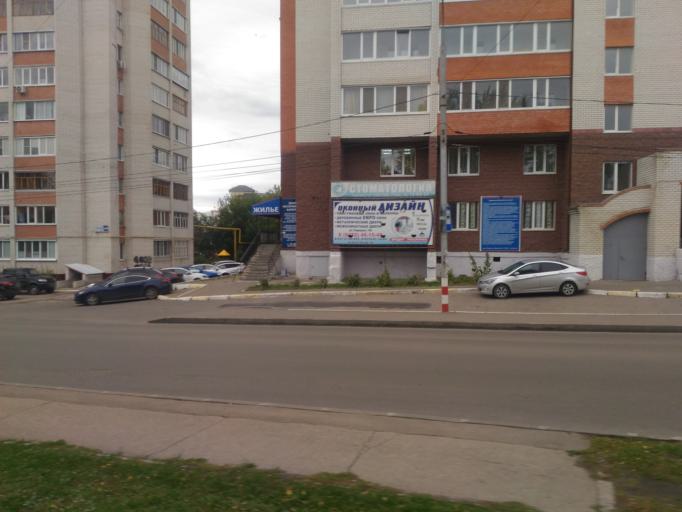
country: RU
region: Ulyanovsk
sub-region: Ulyanovskiy Rayon
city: Ulyanovsk
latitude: 54.3393
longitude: 48.3978
